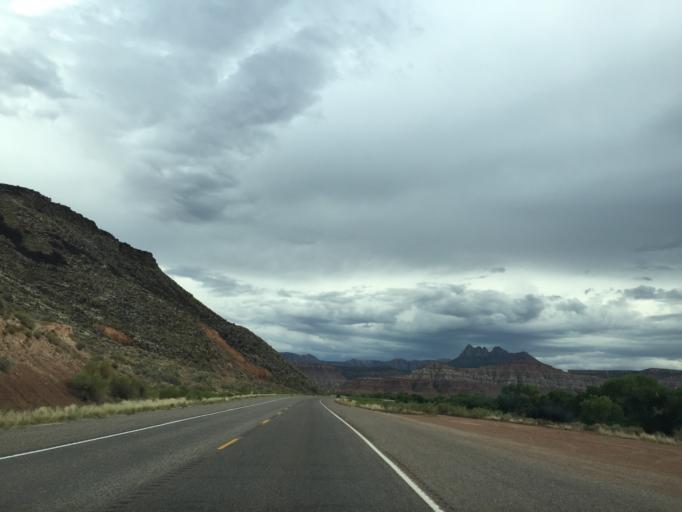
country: US
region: Utah
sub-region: Washington County
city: LaVerkin
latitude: 37.1882
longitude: -113.1402
